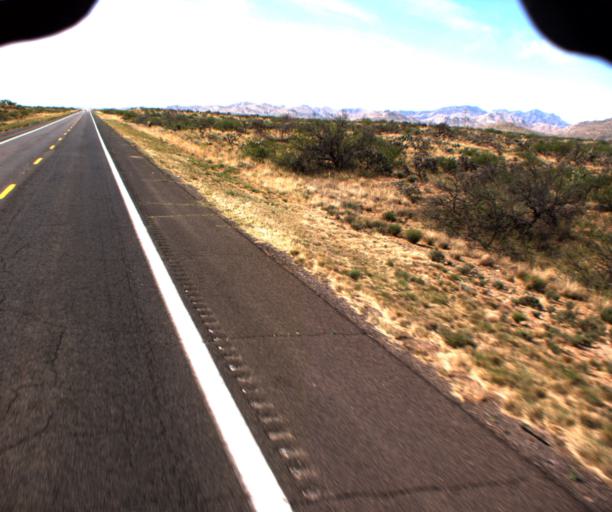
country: US
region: Arizona
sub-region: Graham County
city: Swift Trail Junction
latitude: 32.6170
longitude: -109.6884
